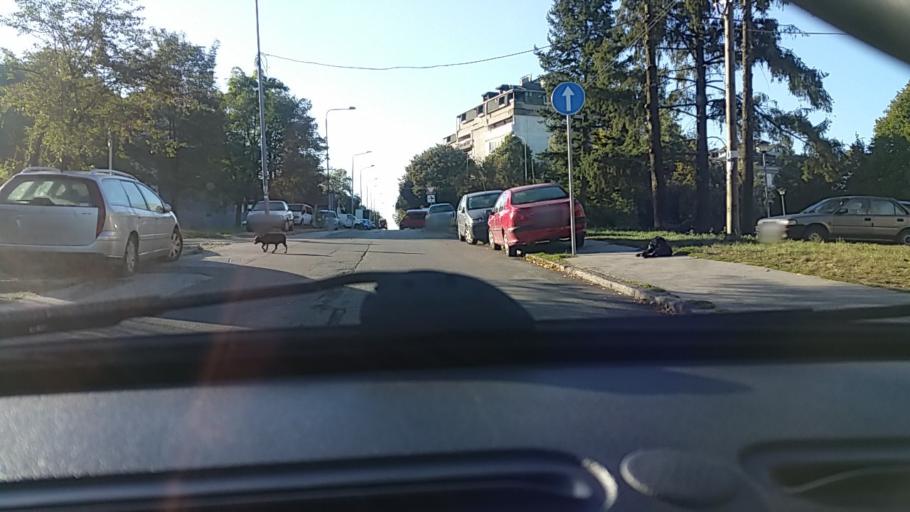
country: RS
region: Central Serbia
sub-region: Belgrade
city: Rakovica
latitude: 44.7489
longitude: 20.4604
